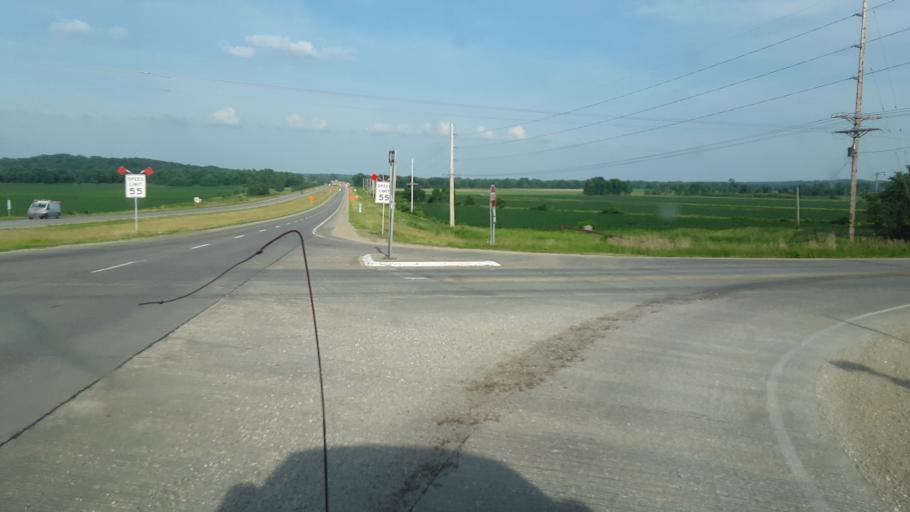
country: US
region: Iowa
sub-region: Tama County
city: Toledo
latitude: 42.0049
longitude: -92.7300
